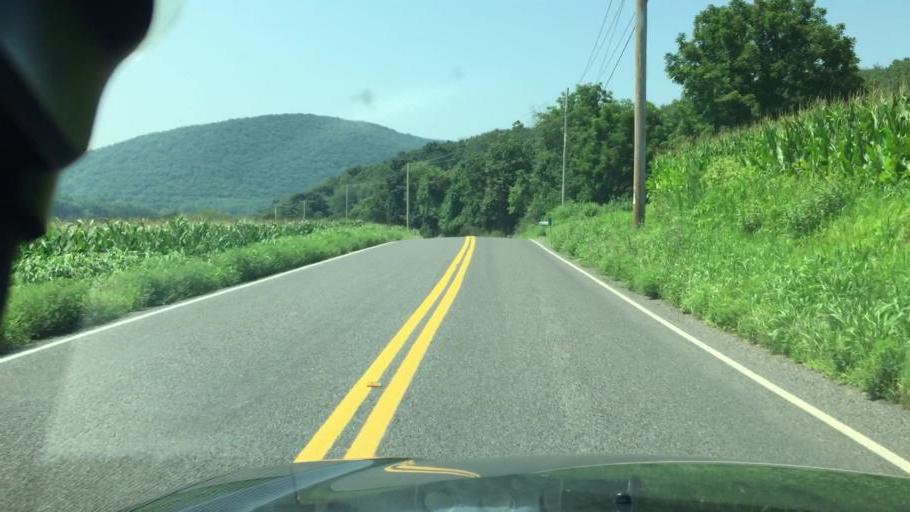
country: US
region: Pennsylvania
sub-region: Columbia County
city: Almedia
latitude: 40.9836
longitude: -76.3640
